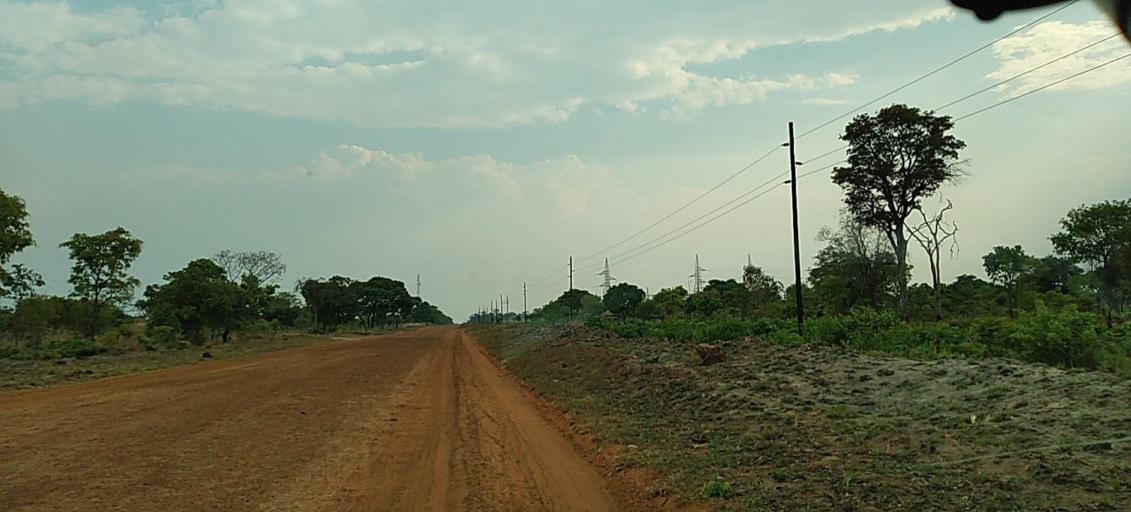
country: ZM
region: North-Western
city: Kabompo
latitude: -13.8753
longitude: 23.6661
